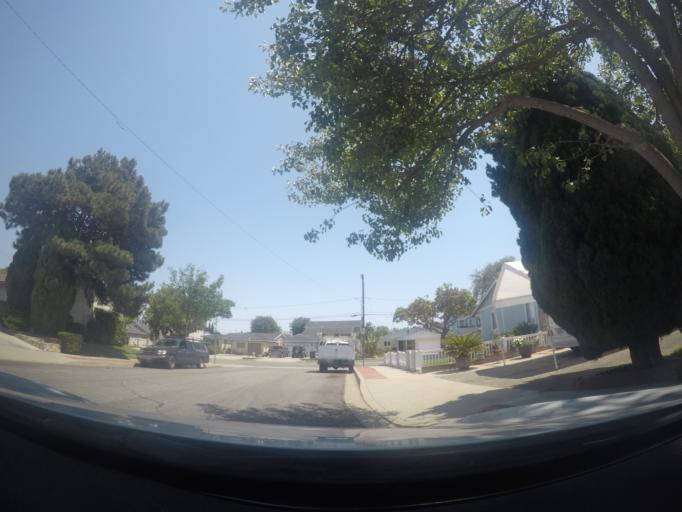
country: US
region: California
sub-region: Los Angeles County
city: Rolling Hills Estates
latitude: 33.8167
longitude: -118.3646
